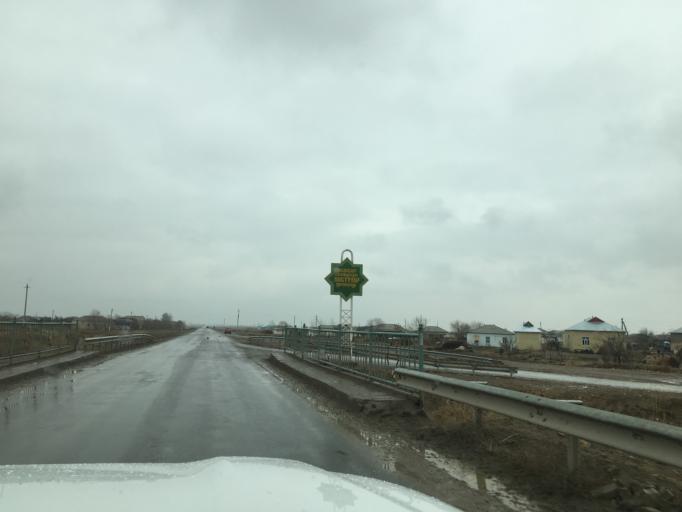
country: TM
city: Murgab
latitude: 37.4694
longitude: 62.0314
